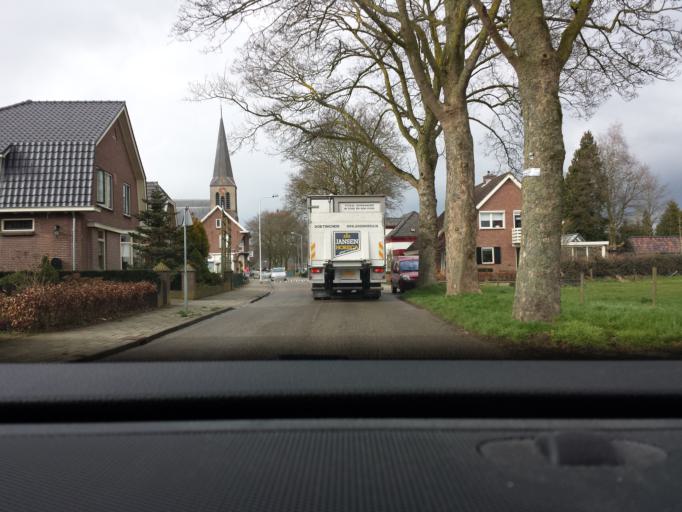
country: NL
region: Gelderland
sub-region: Oude IJsselstreek
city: Wisch
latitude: 51.9380
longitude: 6.3510
